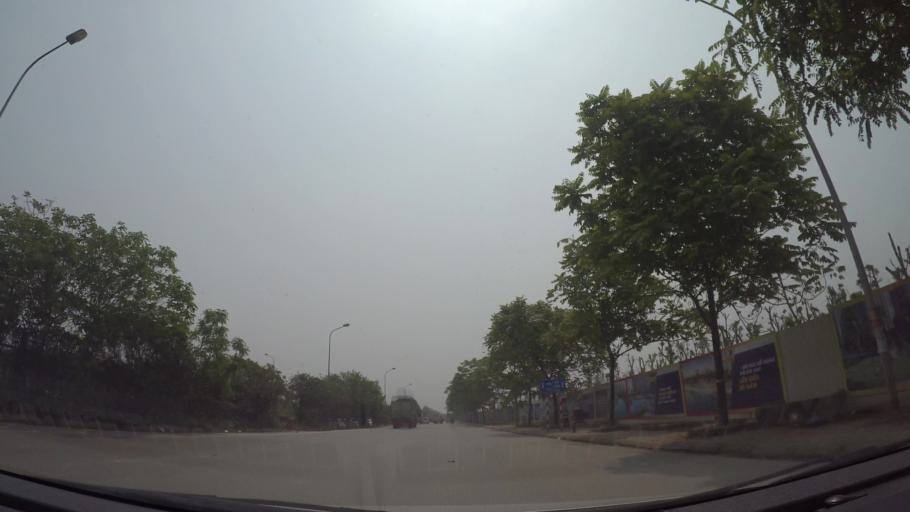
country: VN
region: Ha Noi
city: Cau Dien
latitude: 21.0083
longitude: 105.7514
